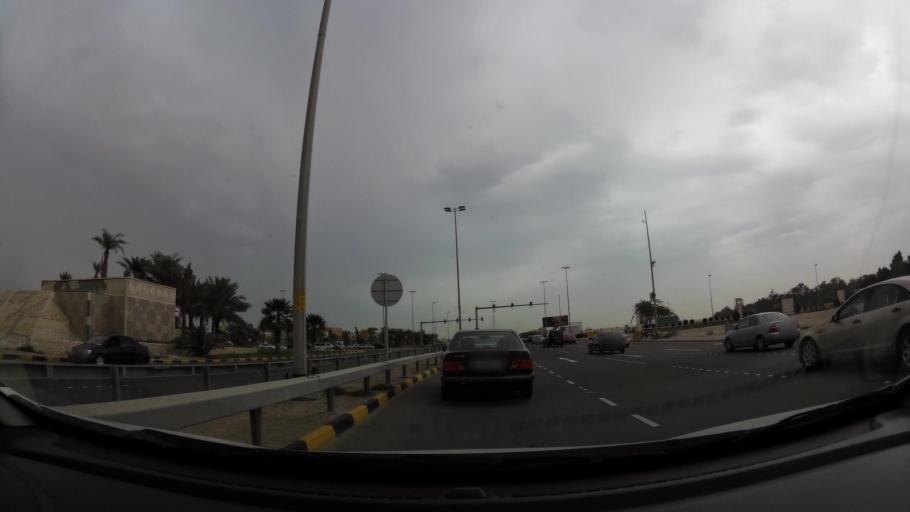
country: BH
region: Central Governorate
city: Dar Kulayb
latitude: 26.0580
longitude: 50.5077
